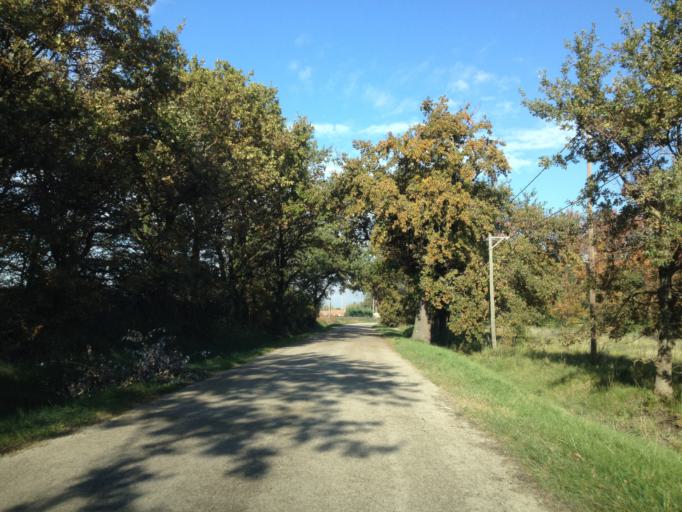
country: FR
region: Provence-Alpes-Cote d'Azur
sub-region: Departement du Vaucluse
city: Courthezon
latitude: 44.0650
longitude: 4.8925
